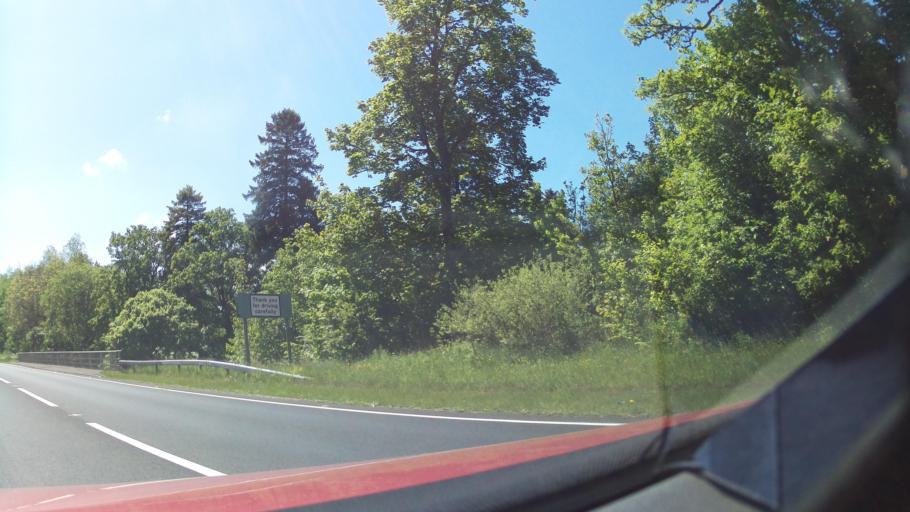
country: GB
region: Scotland
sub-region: The Scottish Borders
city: Hawick
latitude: 55.3376
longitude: -2.9391
